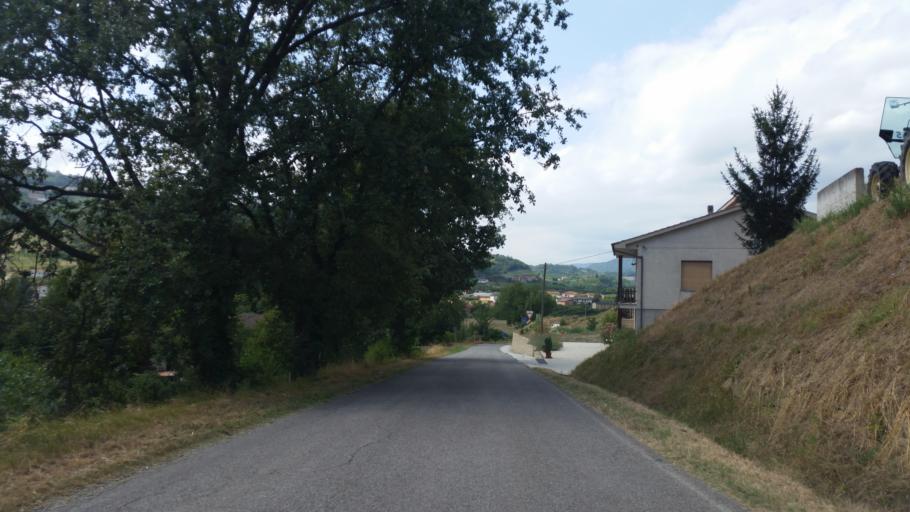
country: IT
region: Piedmont
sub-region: Provincia di Asti
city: Cessole
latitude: 44.6379
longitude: 8.2403
